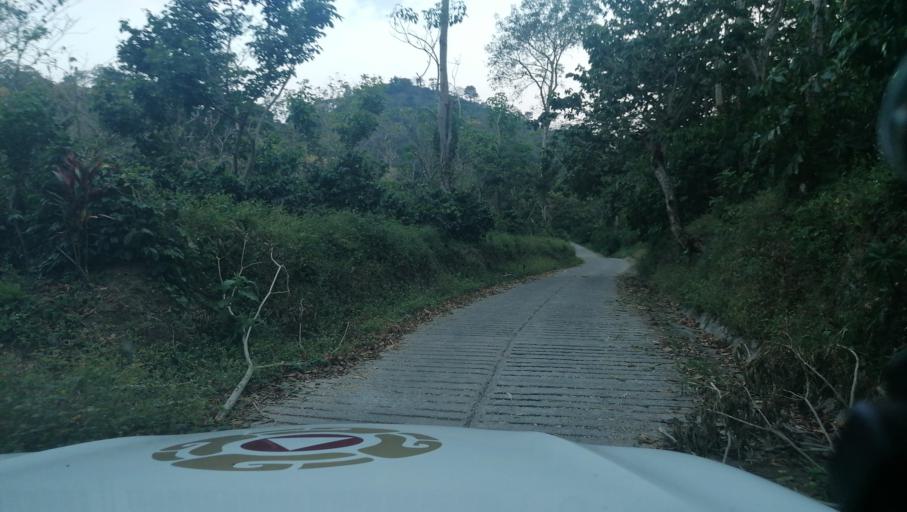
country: MX
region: Chiapas
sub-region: Cacahoatan
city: Benito Juarez
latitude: 15.0909
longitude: -92.2190
